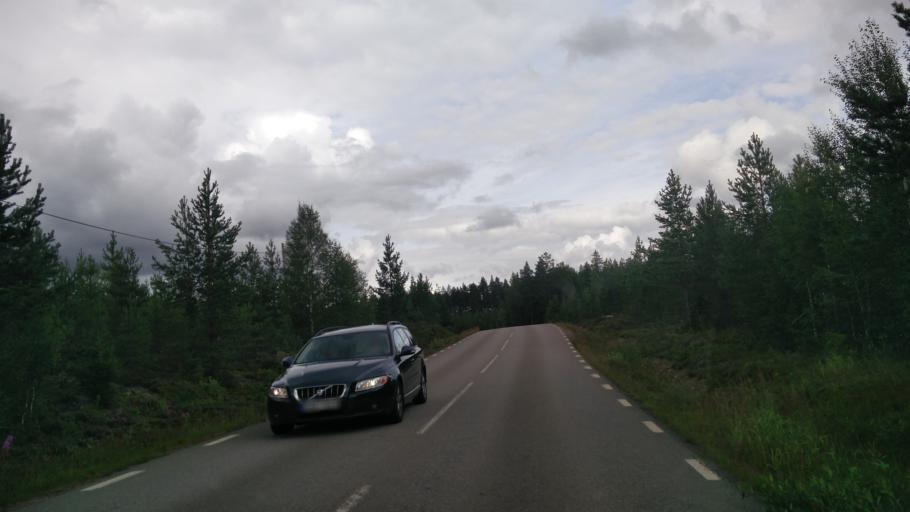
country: NO
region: Hedmark
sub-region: Trysil
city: Innbygda
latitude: 61.1587
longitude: 12.8184
